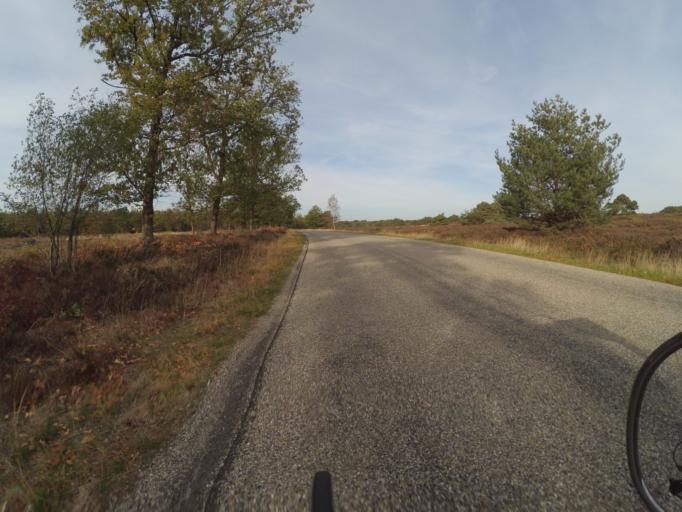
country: NL
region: Overijssel
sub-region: Gemeente Hof van Twente
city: Markelo
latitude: 52.3182
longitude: 6.4126
